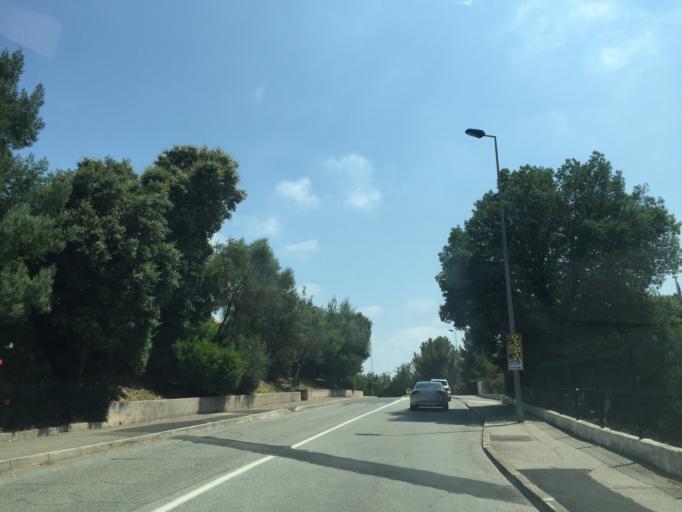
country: FR
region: Provence-Alpes-Cote d'Azur
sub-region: Departement du Var
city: Saint-Raphael
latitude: 43.4327
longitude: 6.8691
